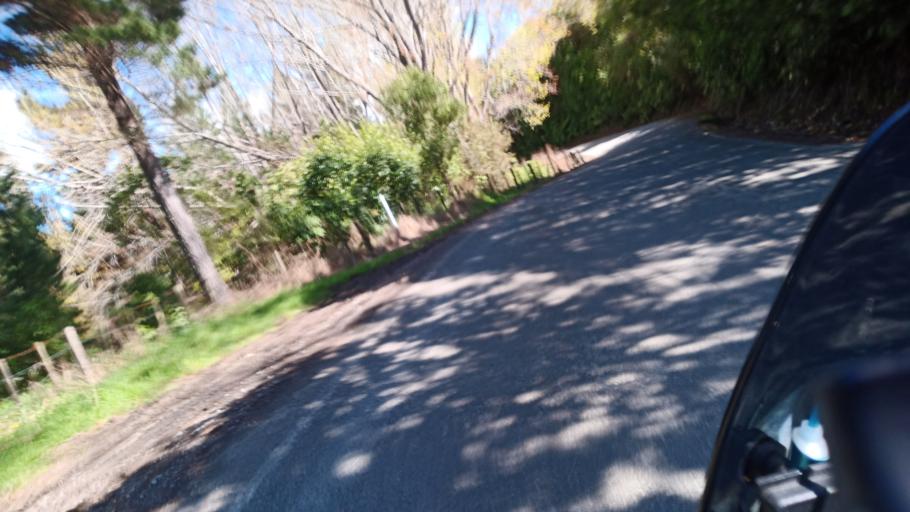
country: NZ
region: Gisborne
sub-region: Gisborne District
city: Gisborne
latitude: -38.7969
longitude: 177.7714
